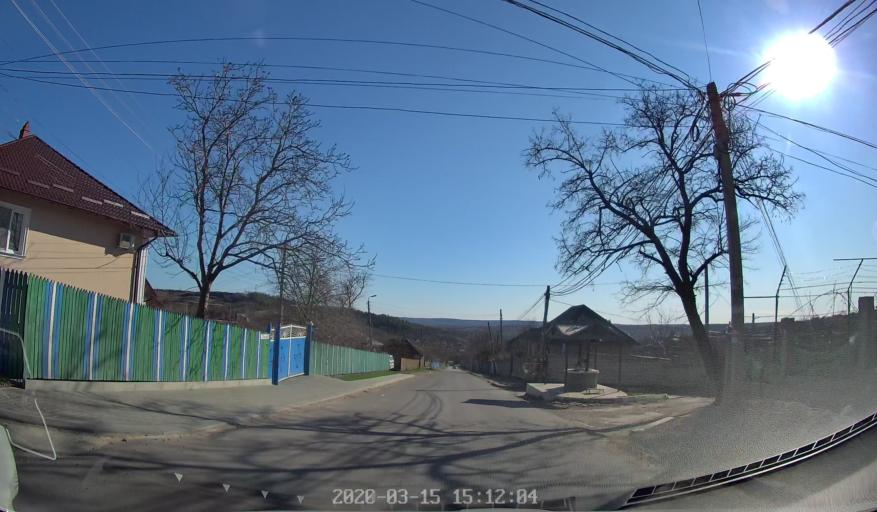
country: MD
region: Orhei
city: Orhei
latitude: 47.2584
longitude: 28.7744
